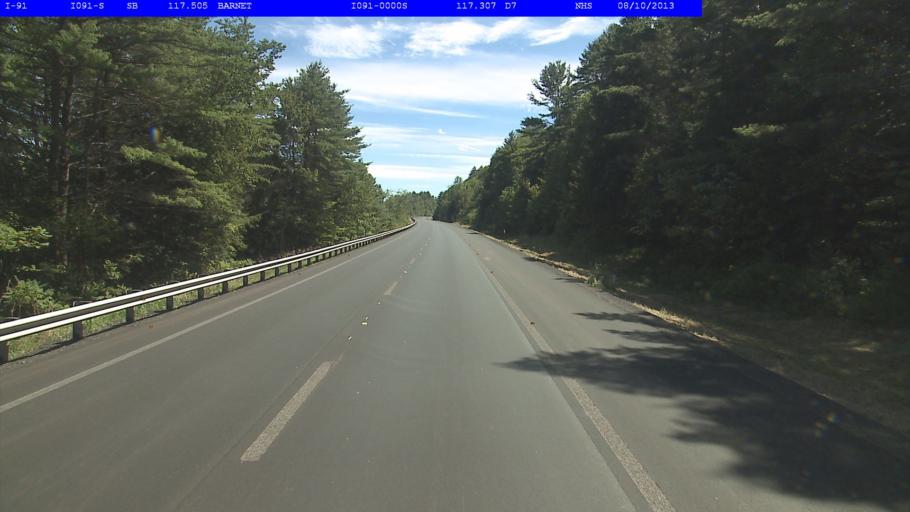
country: US
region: New Hampshire
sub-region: Grafton County
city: Woodsville
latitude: 44.2593
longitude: -72.0662
